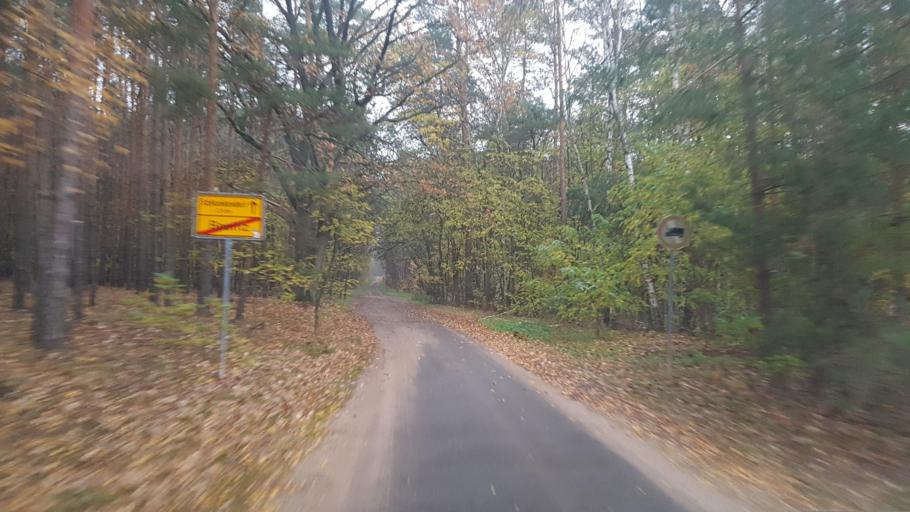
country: DE
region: Brandenburg
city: Beelitz
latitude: 52.2482
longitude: 12.9946
